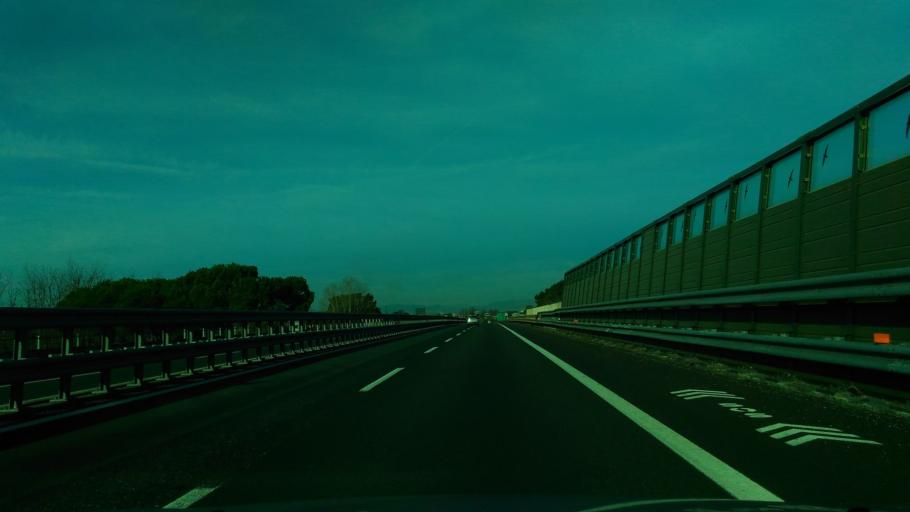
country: IT
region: Tuscany
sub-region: Provincia di Massa-Carrara
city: Massa
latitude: 44.0277
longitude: 10.0928
